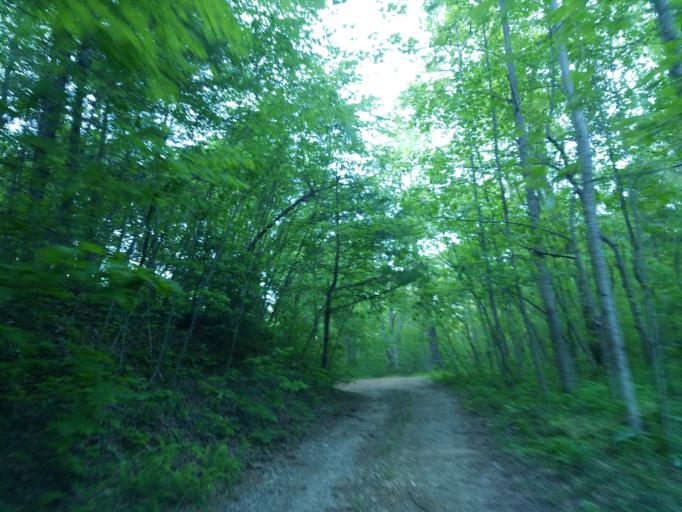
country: US
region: Georgia
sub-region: Lumpkin County
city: Dahlonega
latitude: 34.6692
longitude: -84.1331
